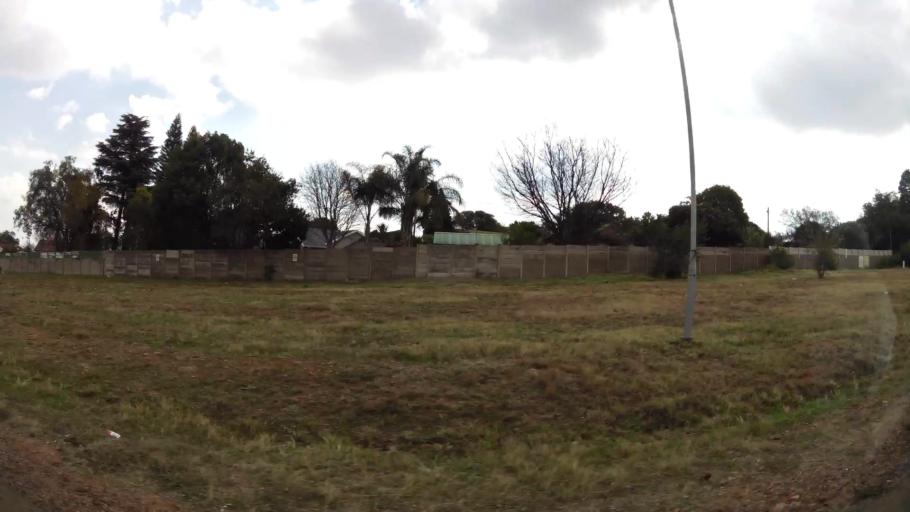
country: ZA
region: Gauteng
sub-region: City of Tshwane Metropolitan Municipality
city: Centurion
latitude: -25.8327
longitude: 28.2543
